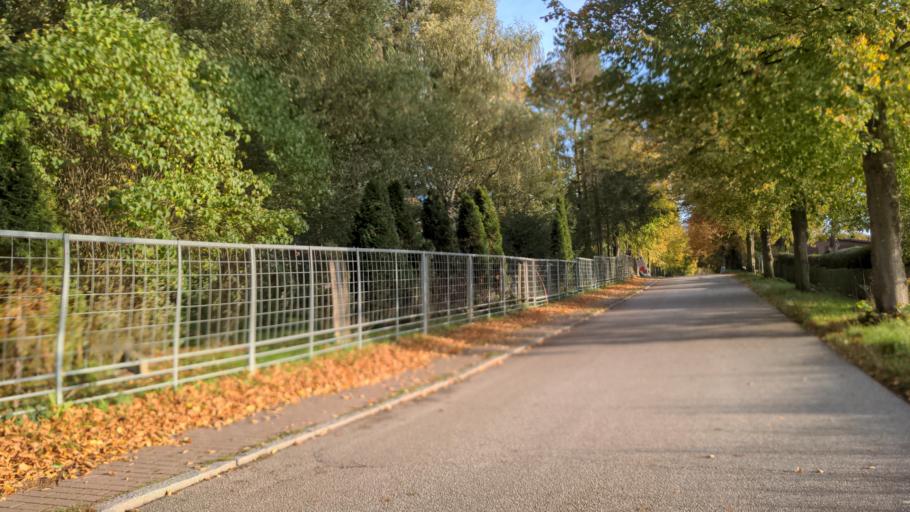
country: DE
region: Schleswig-Holstein
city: Manhagen
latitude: 54.1949
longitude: 10.9382
